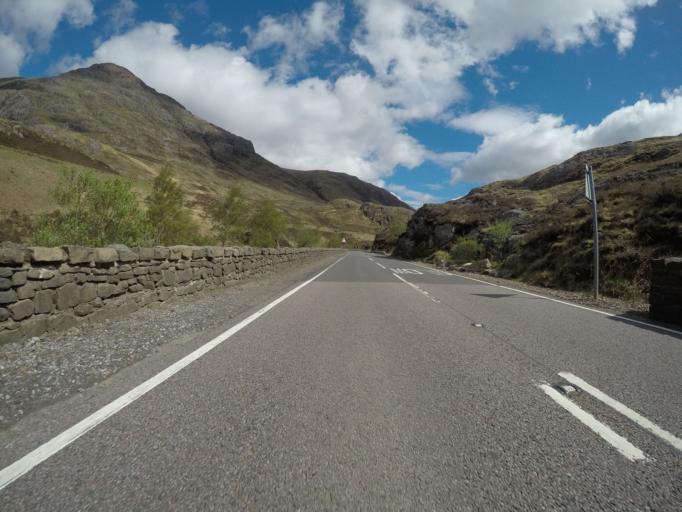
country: GB
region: Scotland
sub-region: Highland
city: Fort William
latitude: 56.6633
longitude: -4.9643
